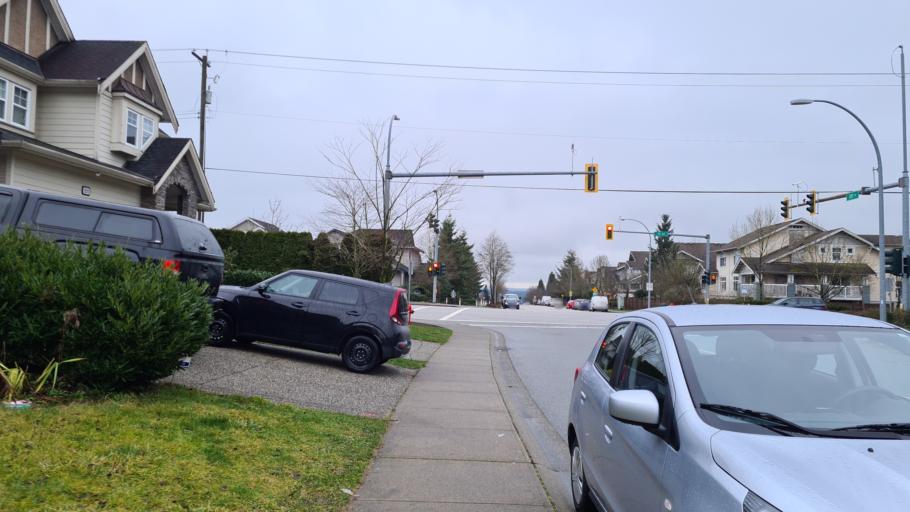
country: CA
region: British Columbia
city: Langley
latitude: 49.1340
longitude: -122.6645
